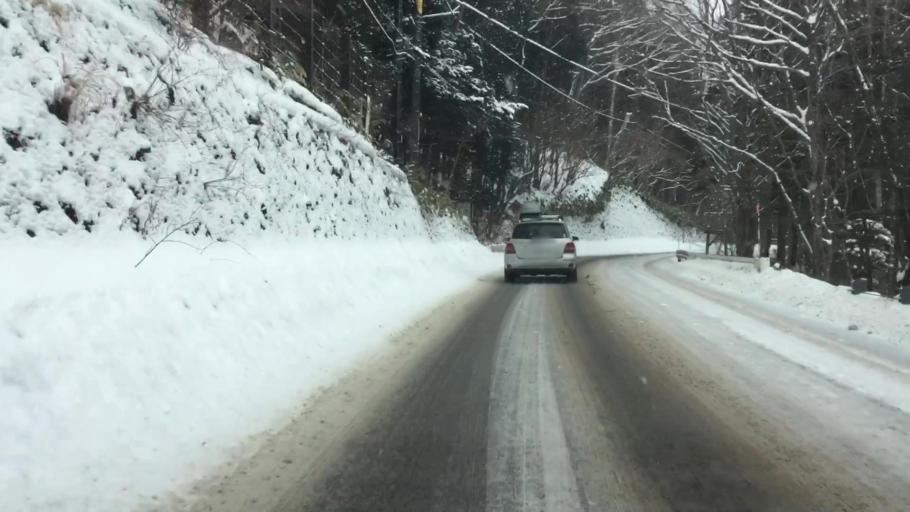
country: JP
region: Tochigi
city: Yaita
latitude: 36.9582
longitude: 139.7790
